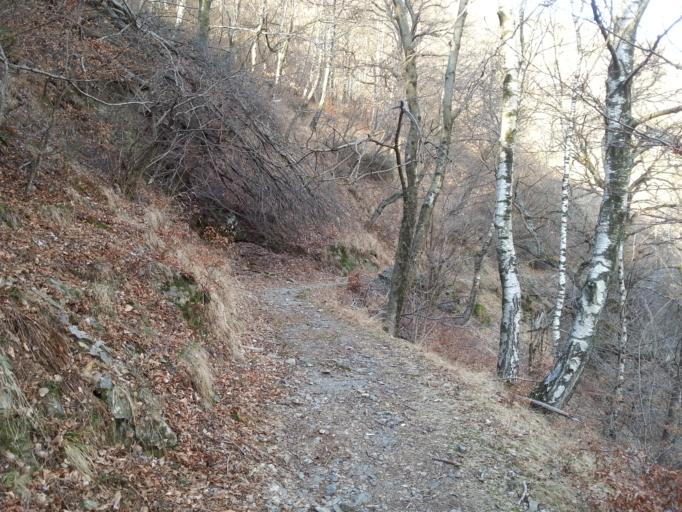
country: CH
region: Ticino
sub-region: Lugano District
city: Gravesano
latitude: 46.0510
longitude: 8.8760
